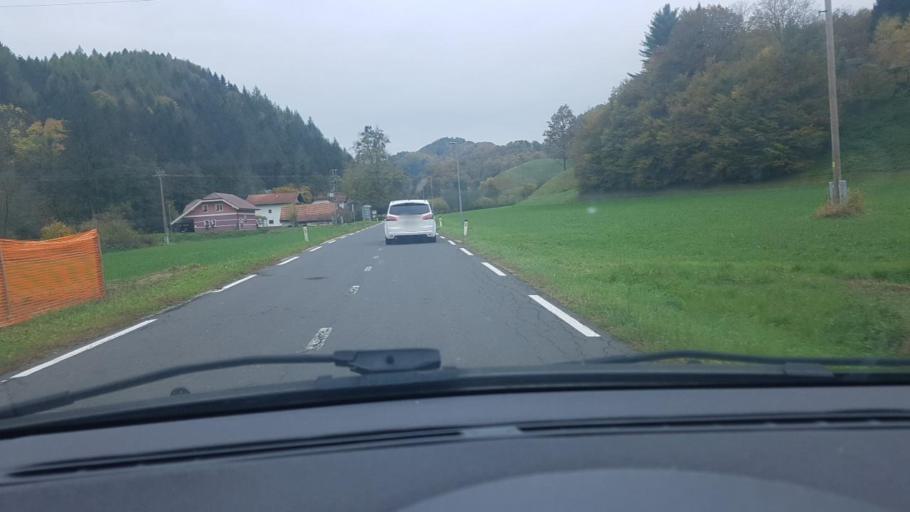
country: SI
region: Makole
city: Makole
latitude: 46.2860
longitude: 15.7145
